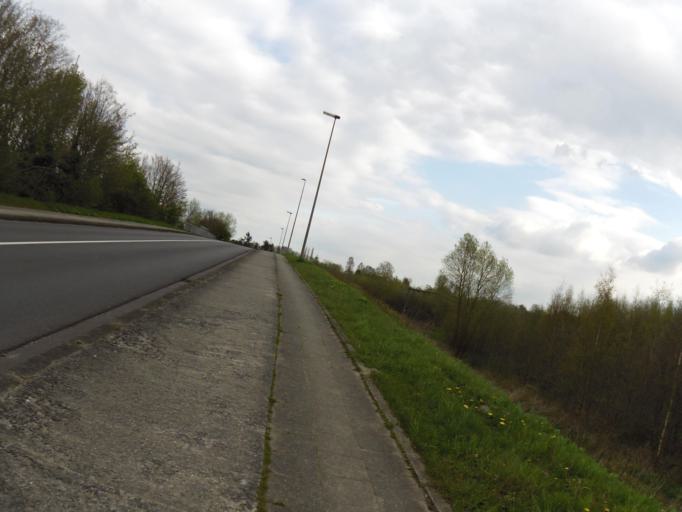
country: BE
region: Flanders
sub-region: Provincie Oost-Vlaanderen
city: De Pinte
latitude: 51.0089
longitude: 3.6693
